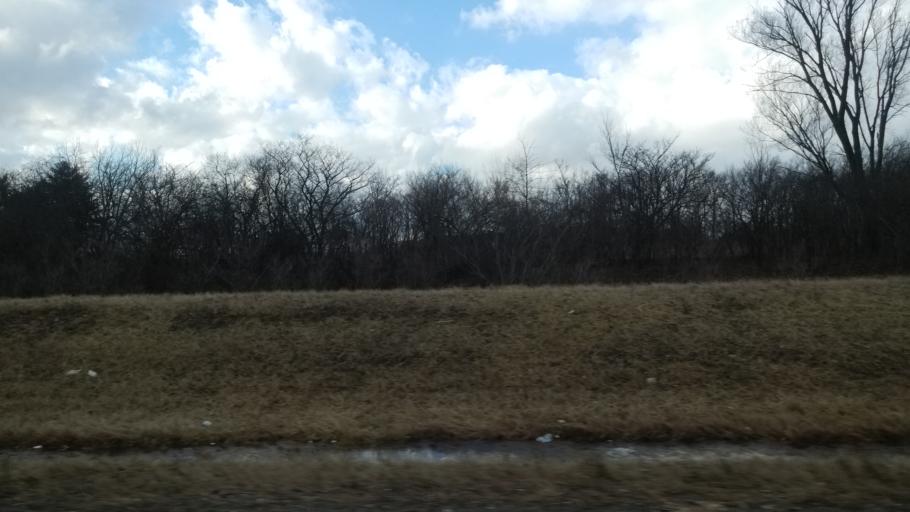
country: US
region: Ohio
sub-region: Lucas County
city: Maumee
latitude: 41.5463
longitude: -83.6962
